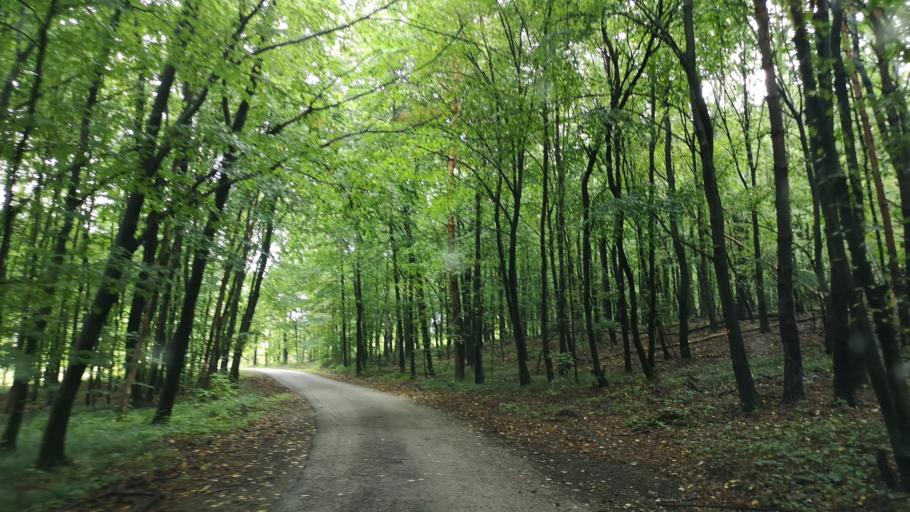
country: SK
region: Trnavsky
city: Smolenice
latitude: 48.5746
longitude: 17.4318
